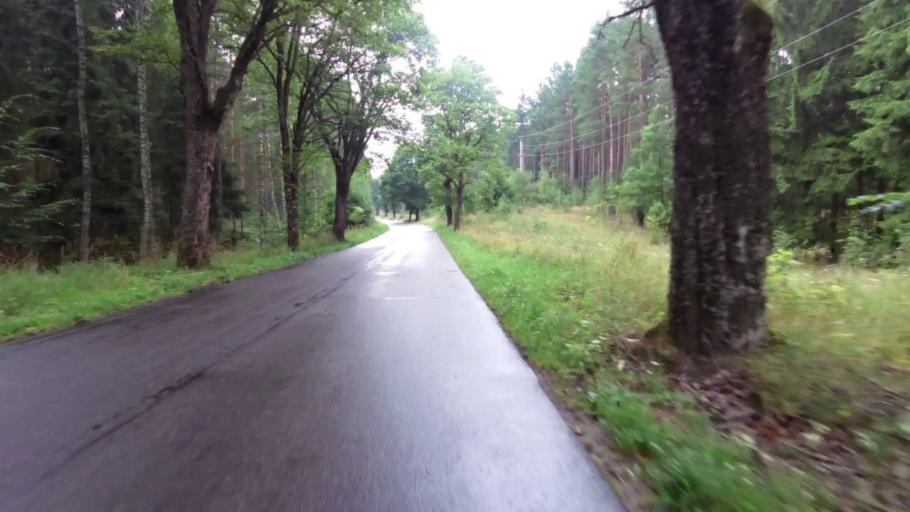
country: PL
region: West Pomeranian Voivodeship
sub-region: Powiat szczecinecki
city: Lubowo
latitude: 53.6030
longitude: 16.3648
